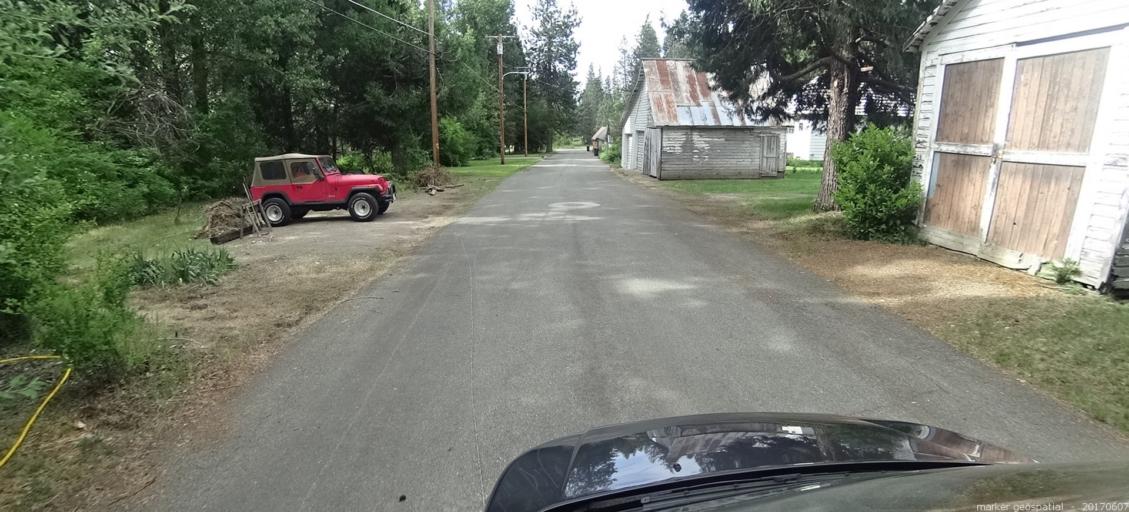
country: US
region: California
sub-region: Siskiyou County
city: McCloud
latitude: 41.2572
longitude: -122.1400
